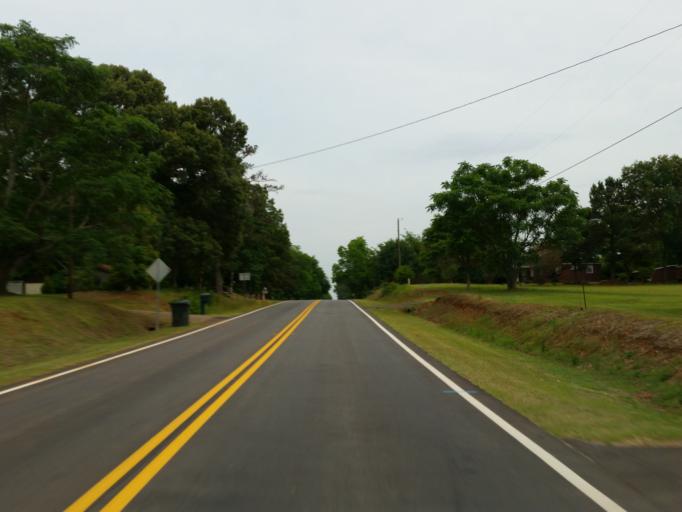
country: US
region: Georgia
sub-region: Dooly County
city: Unadilla
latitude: 32.3322
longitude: -83.7872
